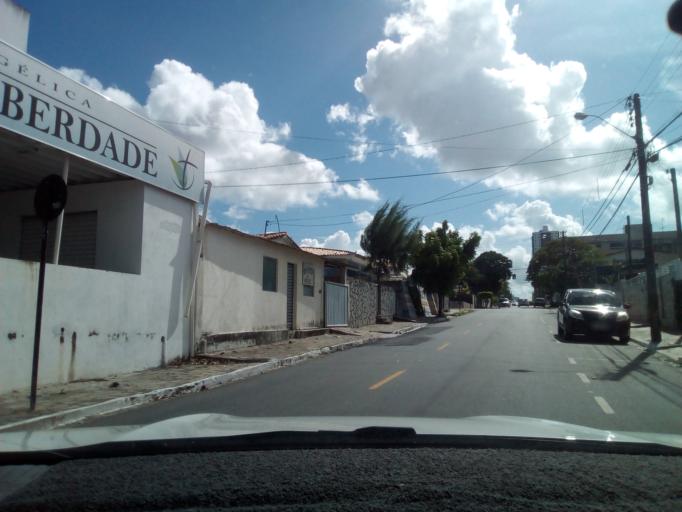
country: BR
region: Paraiba
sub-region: Joao Pessoa
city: Joao Pessoa
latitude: -7.1155
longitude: -34.8482
